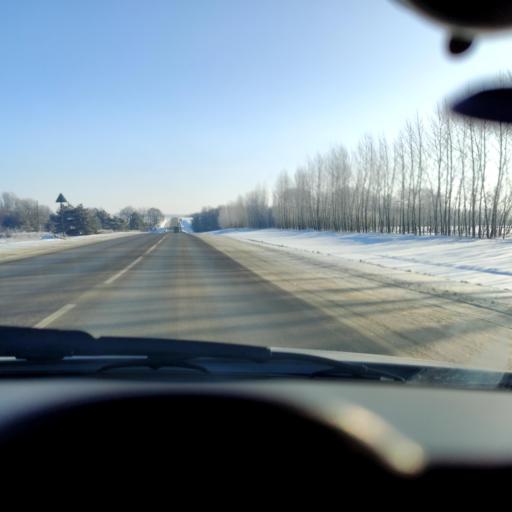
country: RU
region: Kursk
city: Tim
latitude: 51.6529
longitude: 36.9495
